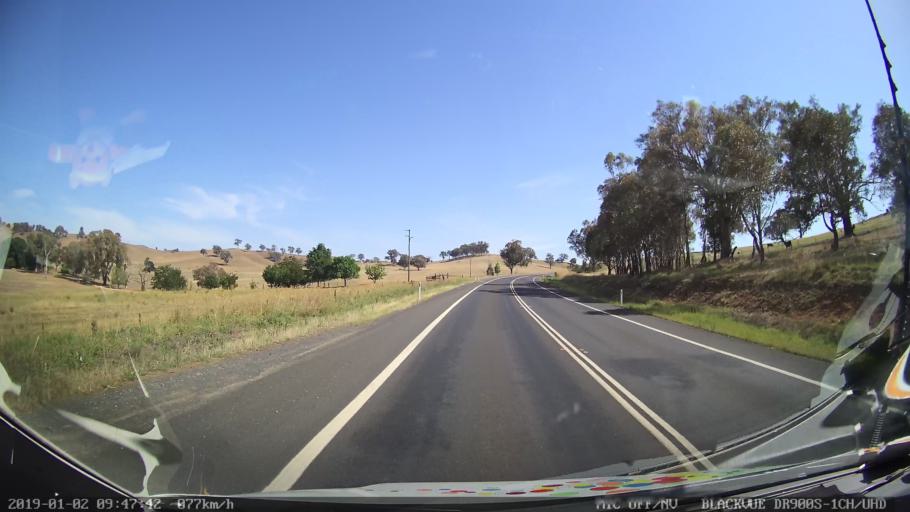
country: AU
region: New South Wales
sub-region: Tumut Shire
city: Tumut
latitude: -35.2817
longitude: 148.2052
